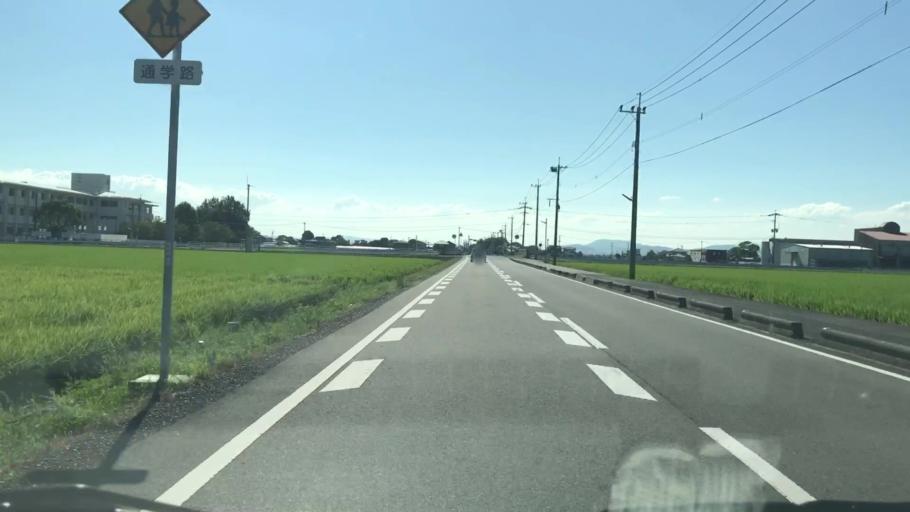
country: JP
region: Saga Prefecture
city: Okawa
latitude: 33.2203
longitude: 130.3477
